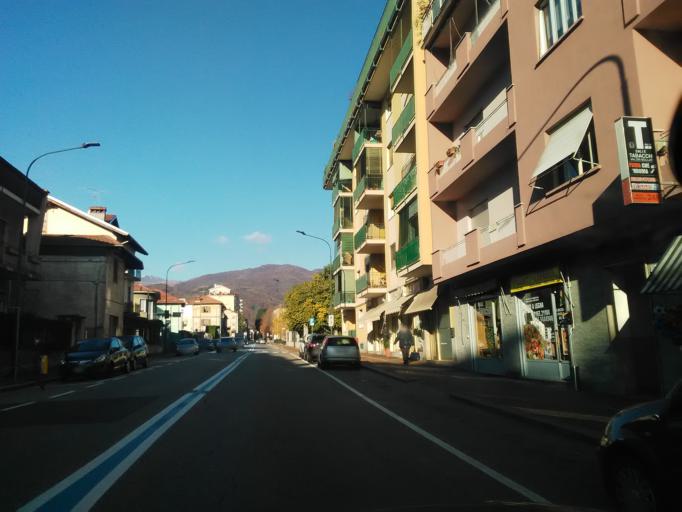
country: IT
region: Piedmont
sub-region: Provincia di Vercelli
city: Borgosesia
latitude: 45.7119
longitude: 8.2859
